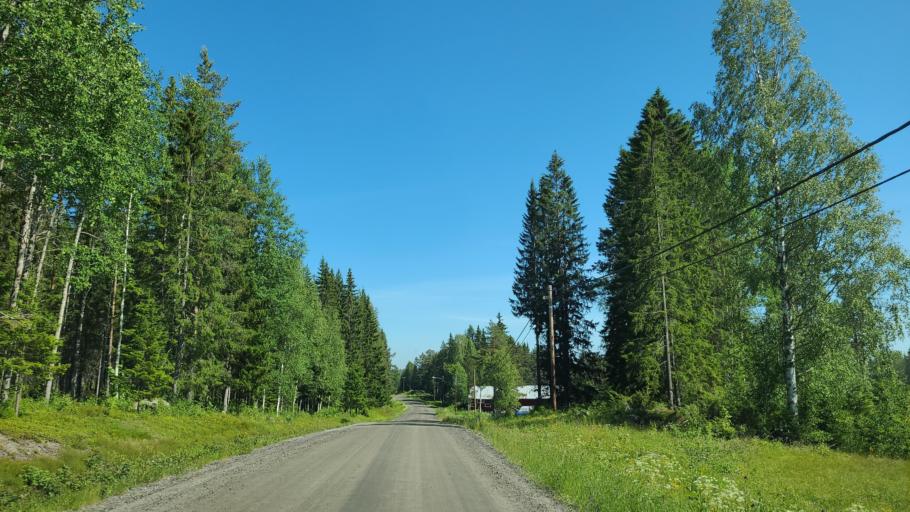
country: SE
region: Vaesterbotten
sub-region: Bjurholms Kommun
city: Bjurholm
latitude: 63.6394
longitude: 19.1904
